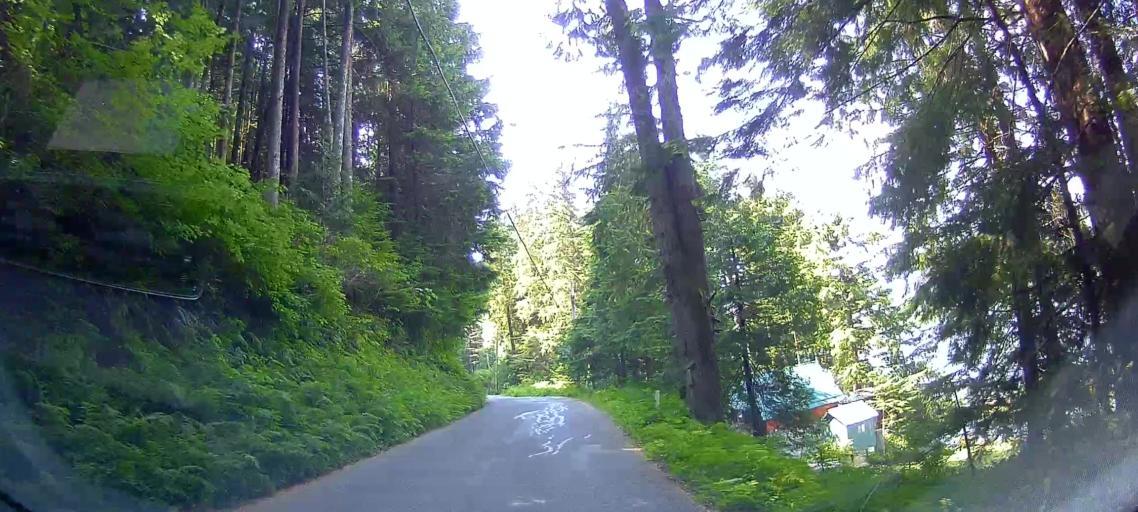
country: US
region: Washington
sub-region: Snohomish County
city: Arlington Heights
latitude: 48.3120
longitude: -121.9959
